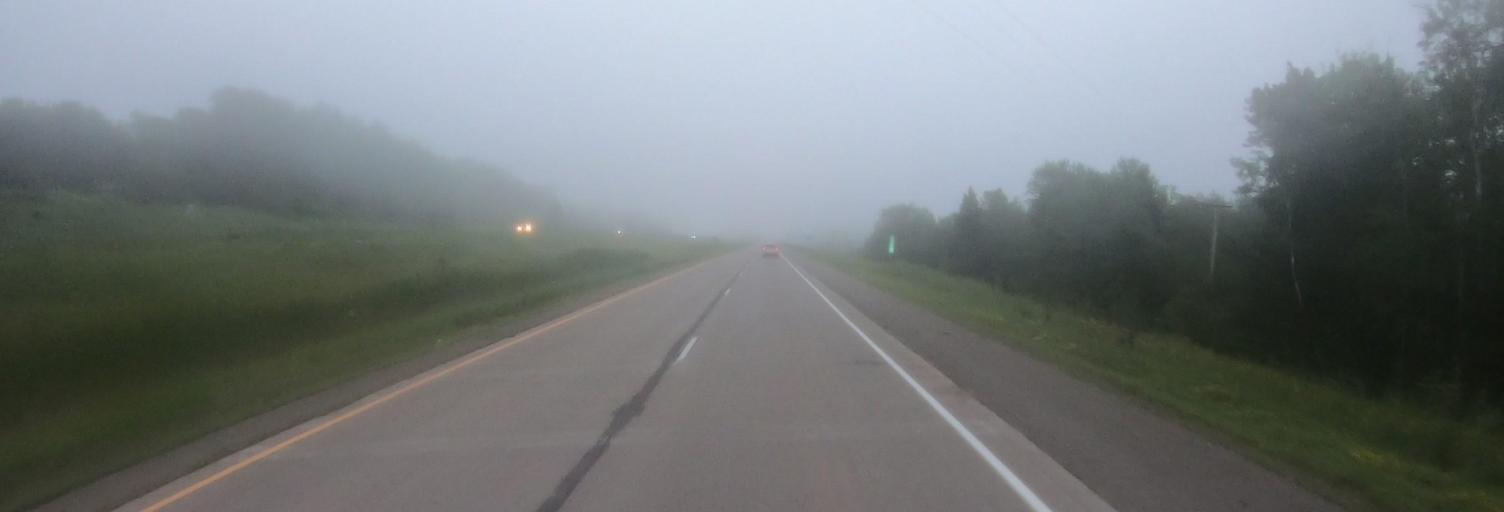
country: US
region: Minnesota
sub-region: Carlton County
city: Moose Lake
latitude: 46.4992
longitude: -92.6844
